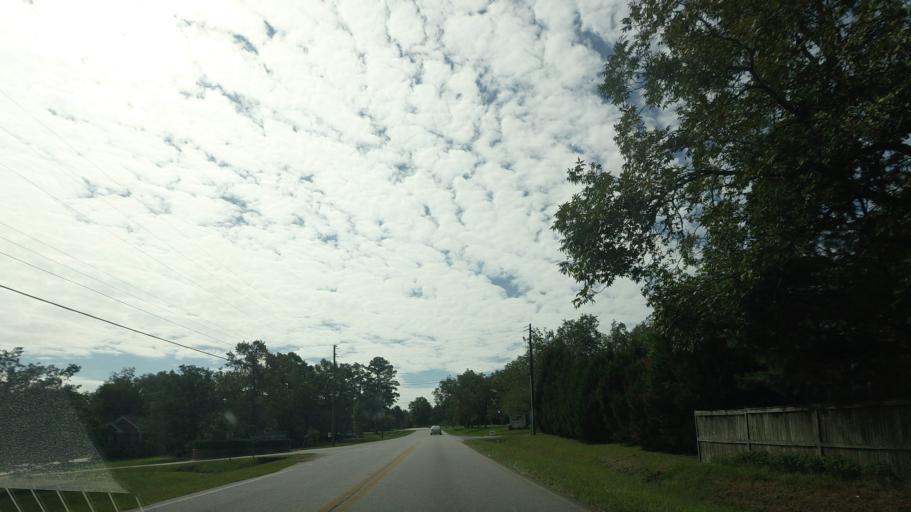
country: US
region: Georgia
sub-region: Houston County
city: Centerville
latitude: 32.6736
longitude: -83.7039
